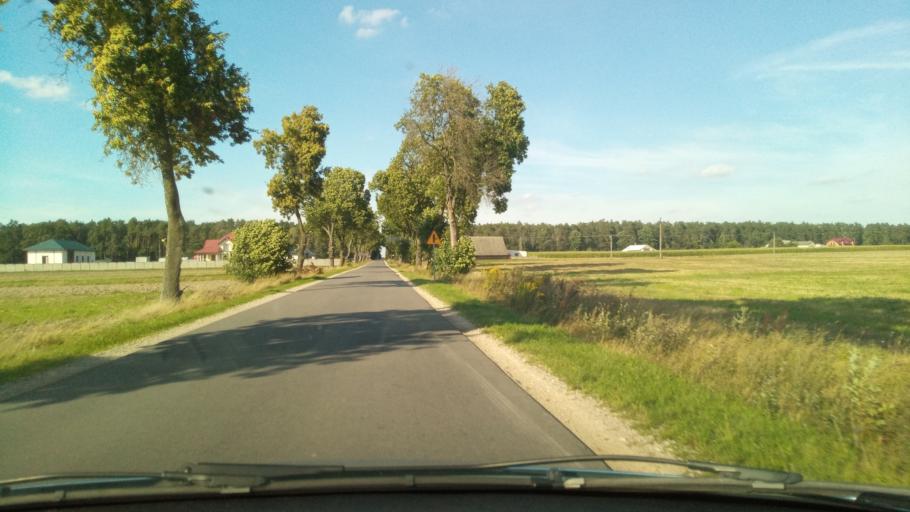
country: PL
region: Lodz Voivodeship
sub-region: Powiat piotrkowski
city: Sulejow
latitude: 51.4042
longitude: 19.8246
